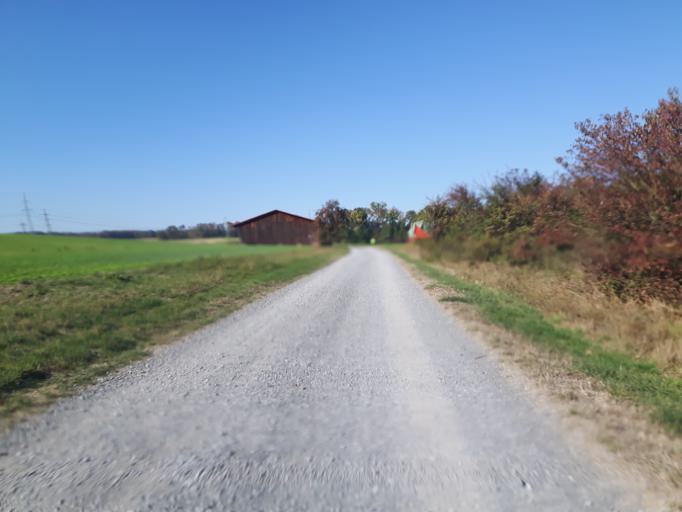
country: DE
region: Baden-Wuerttemberg
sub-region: Regierungsbezirk Stuttgart
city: Leingarten
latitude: 49.1629
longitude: 9.1415
